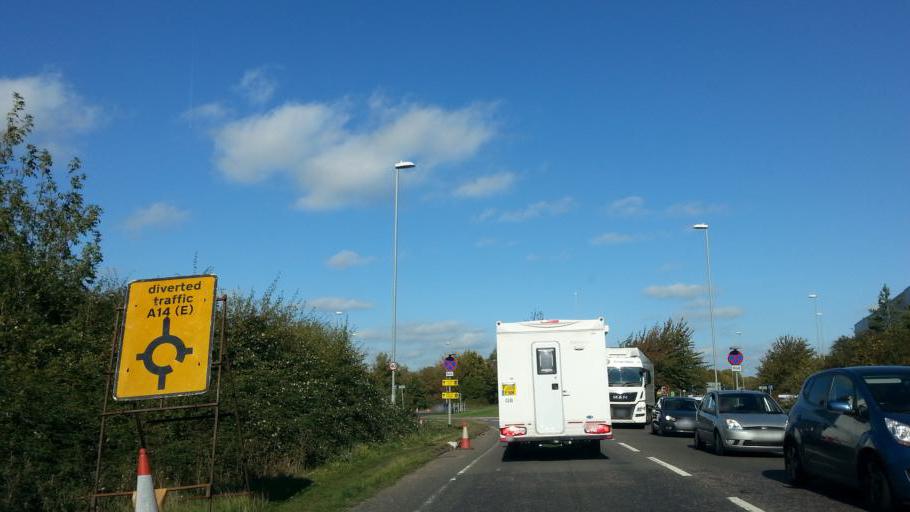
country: GB
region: England
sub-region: Northamptonshire
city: Thrapston
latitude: 52.3935
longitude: -0.5232
